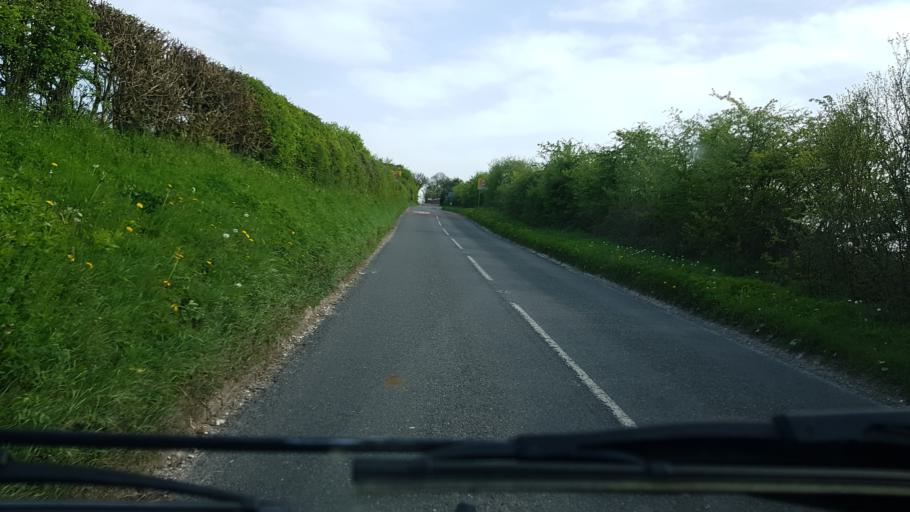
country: GB
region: England
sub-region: Hampshire
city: Overton
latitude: 51.2550
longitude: -1.2648
